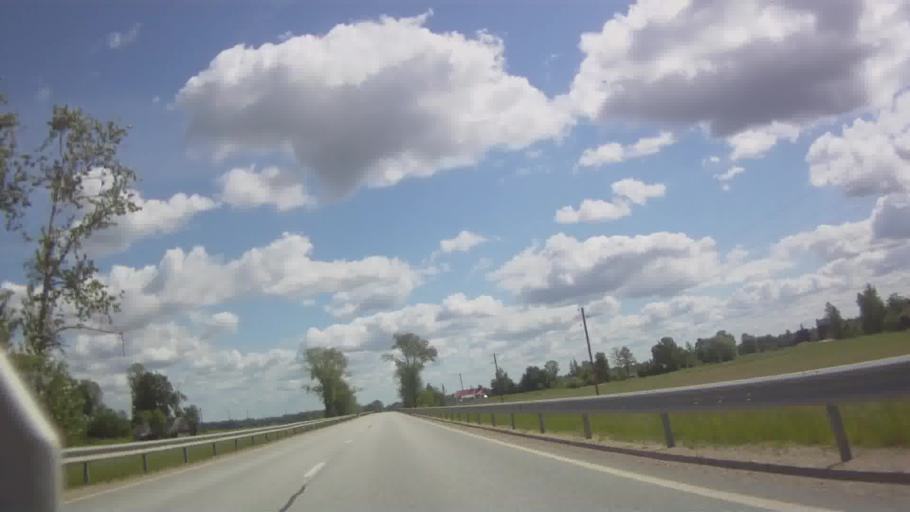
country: LV
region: Livani
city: Livani
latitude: 56.5345
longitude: 26.3138
